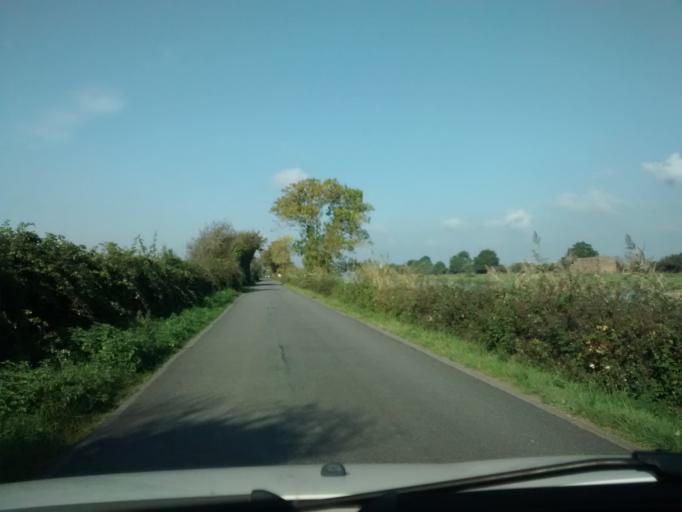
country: FR
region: Pays de la Loire
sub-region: Departement de la Loire-Atlantique
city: Frossay
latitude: 47.2480
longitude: -1.8939
